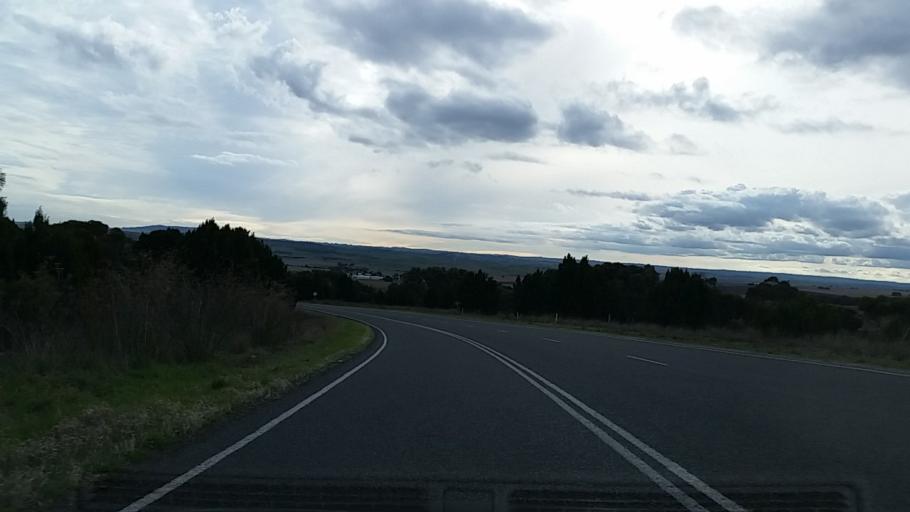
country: AU
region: South Australia
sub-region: Mount Barker
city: Callington
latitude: -35.1133
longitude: 139.0654
